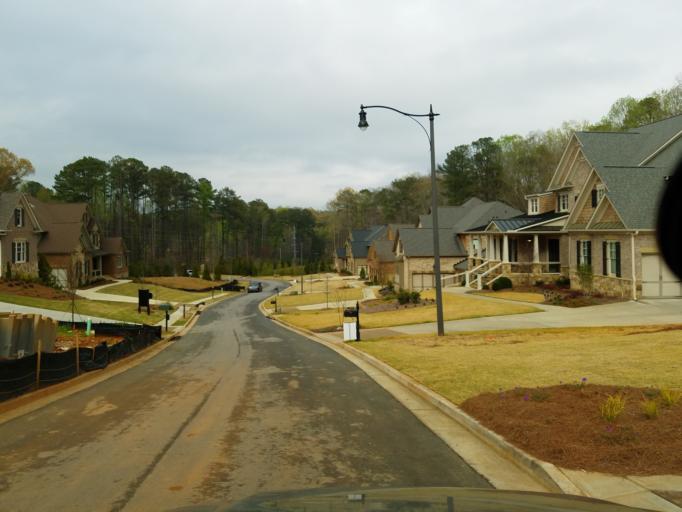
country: US
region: Georgia
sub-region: Fulton County
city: Roswell
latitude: 34.0173
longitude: -84.4143
